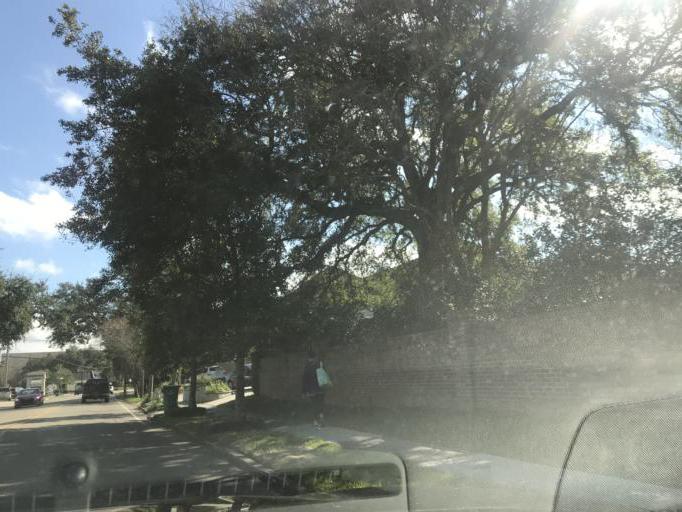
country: US
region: Louisiana
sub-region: Jefferson Parish
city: Metairie
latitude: 29.9891
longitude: -90.1335
